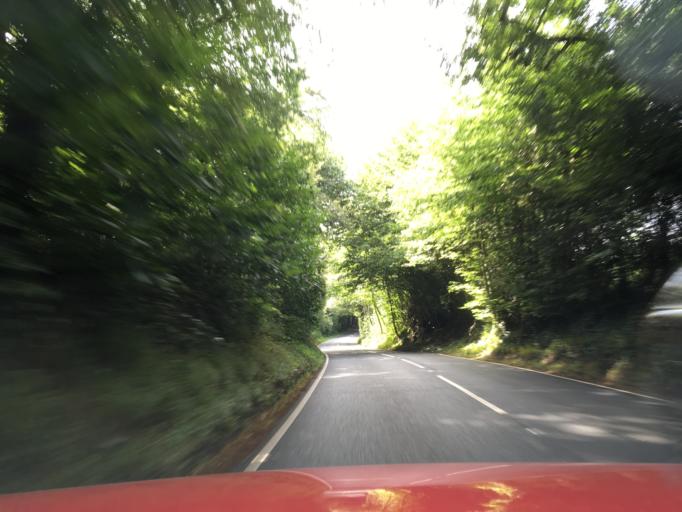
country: GB
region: England
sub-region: East Sussex
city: Forest Row
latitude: 51.1366
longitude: 0.0682
